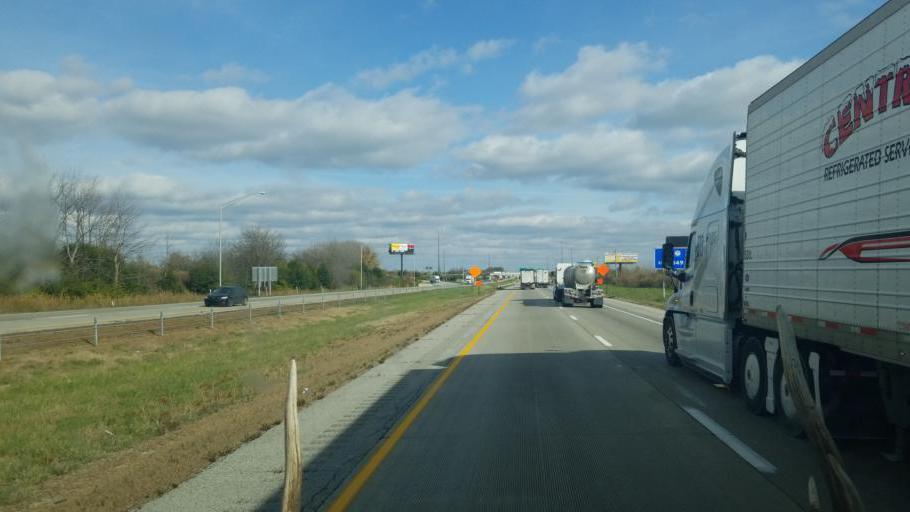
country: US
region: Indiana
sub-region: Wayne County
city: Richmond
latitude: 39.8658
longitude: -84.9368
